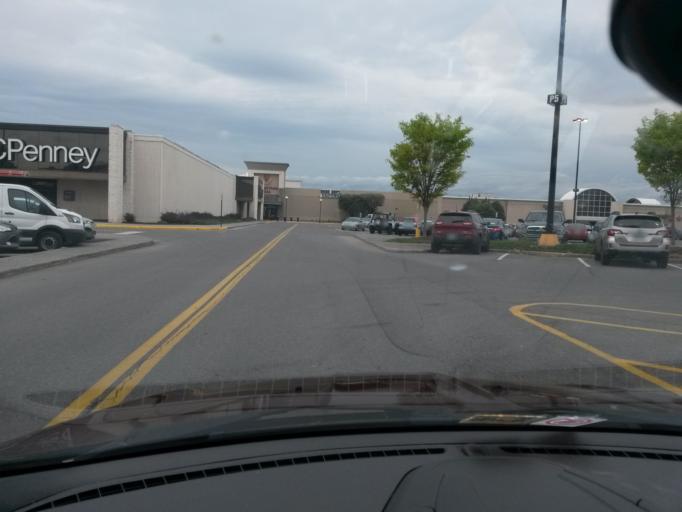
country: US
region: Virginia
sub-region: Roanoke County
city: Hollins
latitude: 37.3057
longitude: -79.9637
